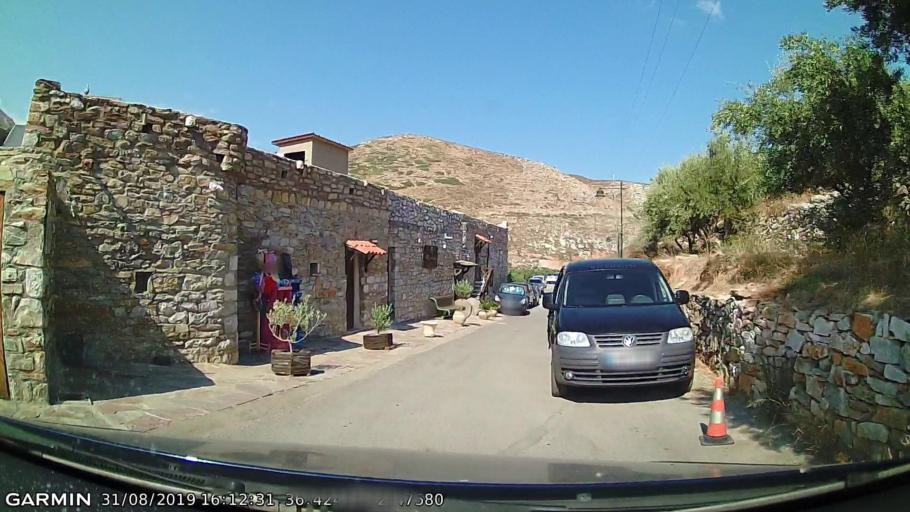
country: GR
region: Peloponnese
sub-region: Nomos Lakonias
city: Gytheio
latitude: 36.4247
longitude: 22.4757
